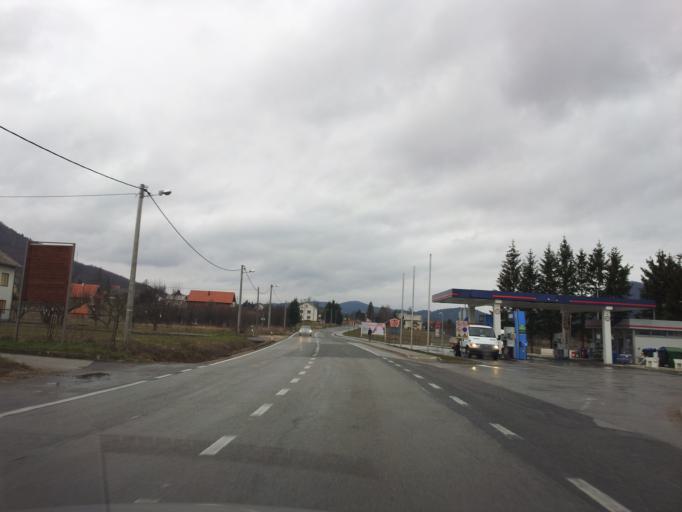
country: BA
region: Federation of Bosnia and Herzegovina
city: Izacic
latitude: 44.7517
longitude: 15.7023
